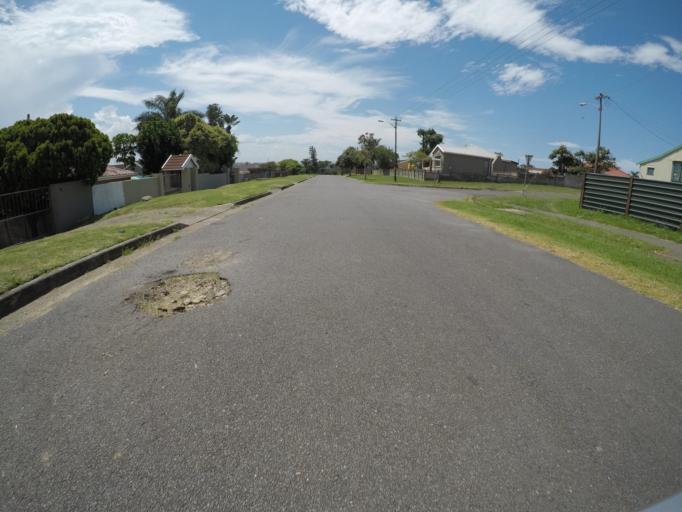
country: ZA
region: Eastern Cape
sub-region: Buffalo City Metropolitan Municipality
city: East London
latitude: -33.0310
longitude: 27.8699
